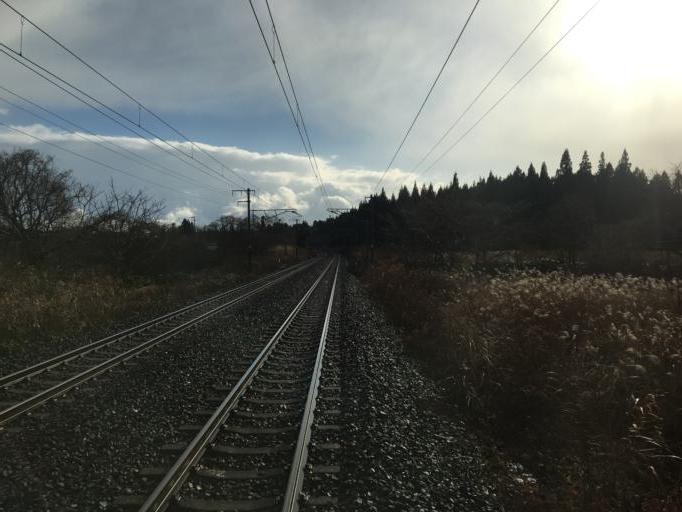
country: JP
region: Aomori
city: Aomori Shi
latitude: 40.9156
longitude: 141.0356
